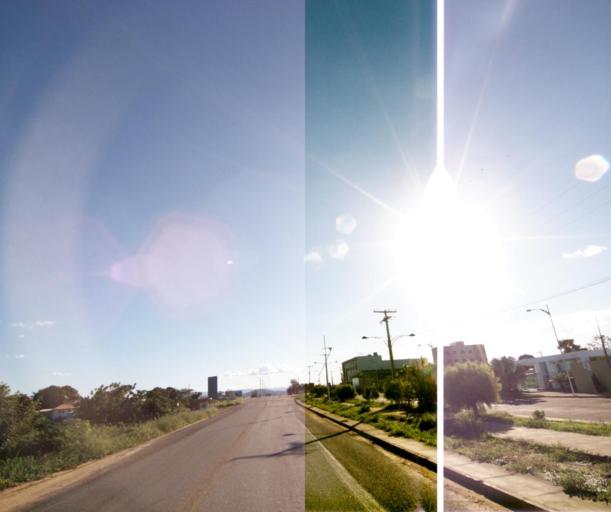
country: BR
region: Bahia
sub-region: Guanambi
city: Guanambi
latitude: -14.2011
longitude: -42.7557
